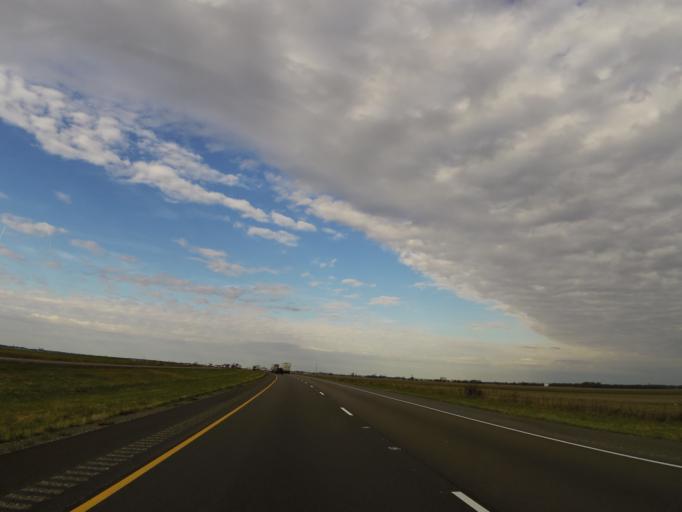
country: US
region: Illinois
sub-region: Washington County
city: Okawville
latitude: 38.4255
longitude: -89.4600
